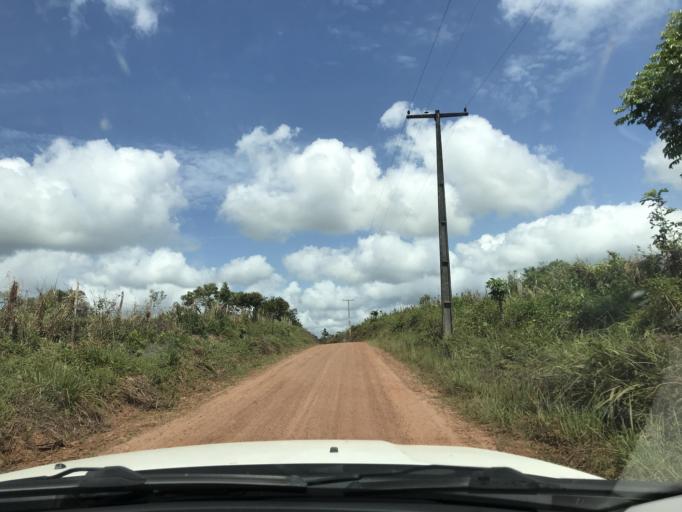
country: BR
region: Bahia
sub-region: Entre Rios
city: Entre Rios
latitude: -12.1857
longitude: -38.0532
